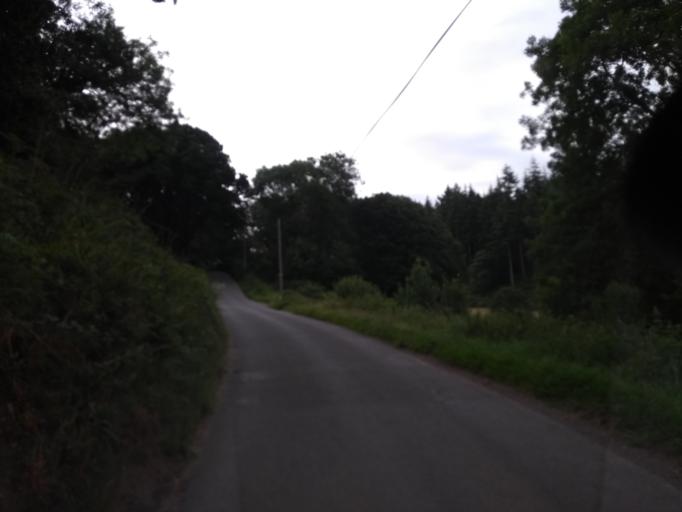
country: GB
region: England
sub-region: Somerset
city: Williton
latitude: 51.1177
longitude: -3.3207
